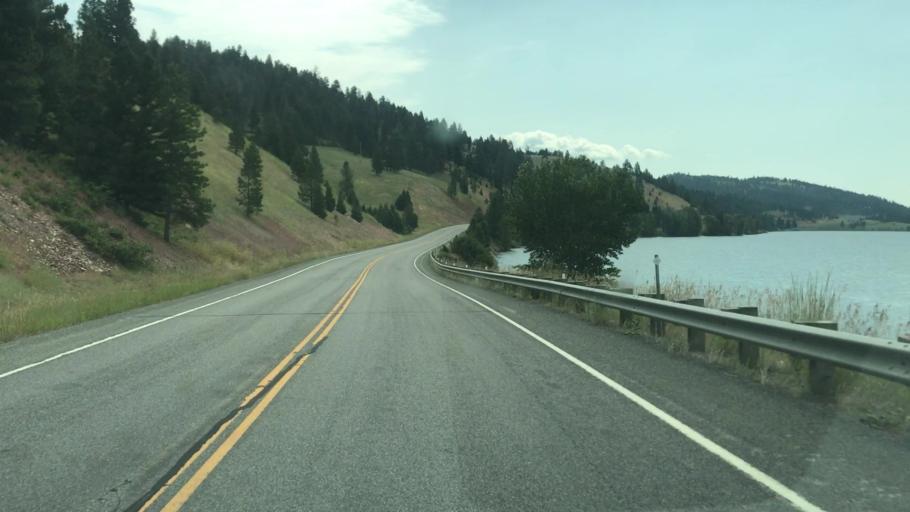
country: US
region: Montana
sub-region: Lewis and Clark County
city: Lincoln
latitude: 46.8009
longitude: -112.8029
